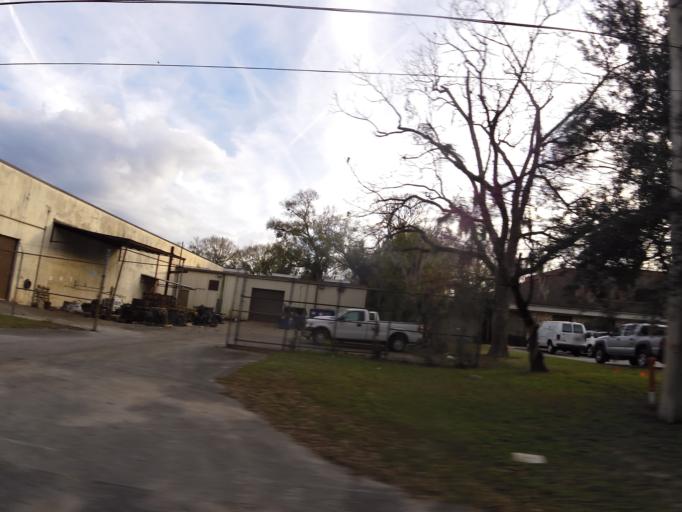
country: US
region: Florida
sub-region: Duval County
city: Jacksonville
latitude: 30.3286
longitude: -81.7447
